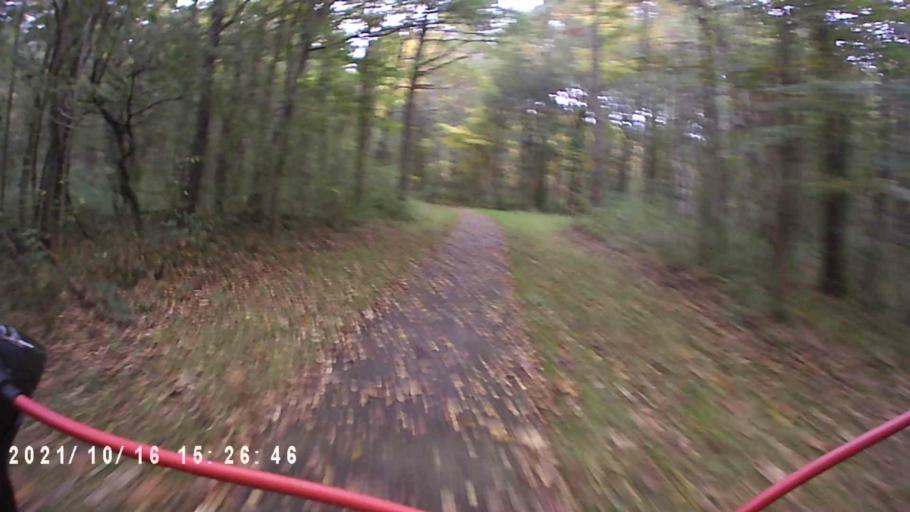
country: NL
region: Friesland
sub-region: Gemeente Dongeradeel
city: Anjum
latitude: 53.4014
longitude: 6.2295
